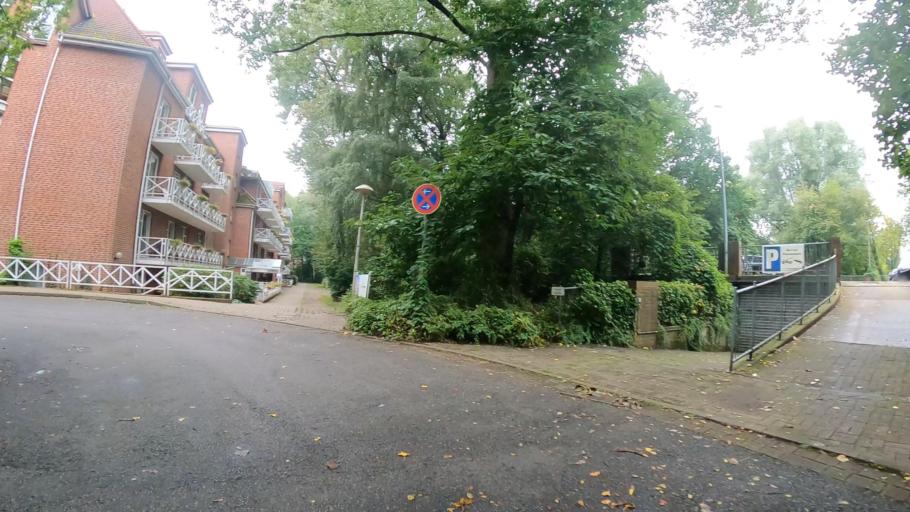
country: DE
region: Schleswig-Holstein
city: Rellingen
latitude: 53.6474
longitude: 9.8085
